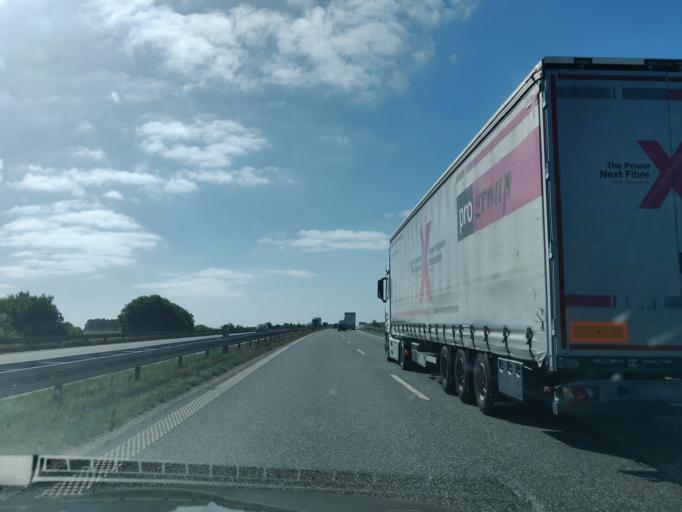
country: DK
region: Central Jutland
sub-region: Randers Kommune
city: Spentrup
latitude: 56.5353
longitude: 9.9232
